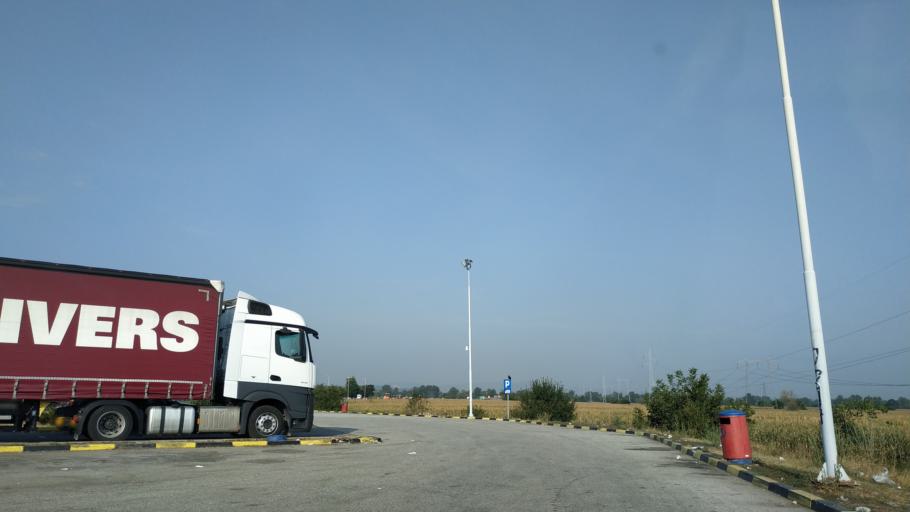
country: RS
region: Central Serbia
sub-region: Pomoravski Okrug
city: Cuprija
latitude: 43.9553
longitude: 21.3639
